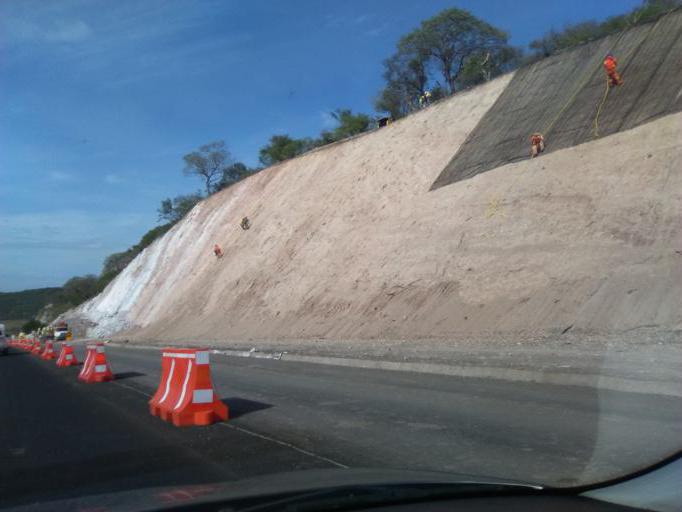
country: MX
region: Morelos
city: Tilzapotla
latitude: 18.4426
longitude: -99.1740
